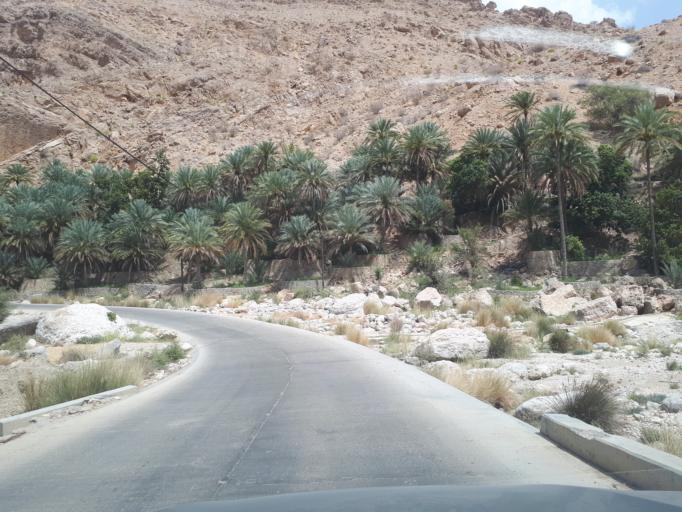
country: OM
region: Ash Sharqiyah
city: Badiyah
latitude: 22.6052
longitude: 59.0876
